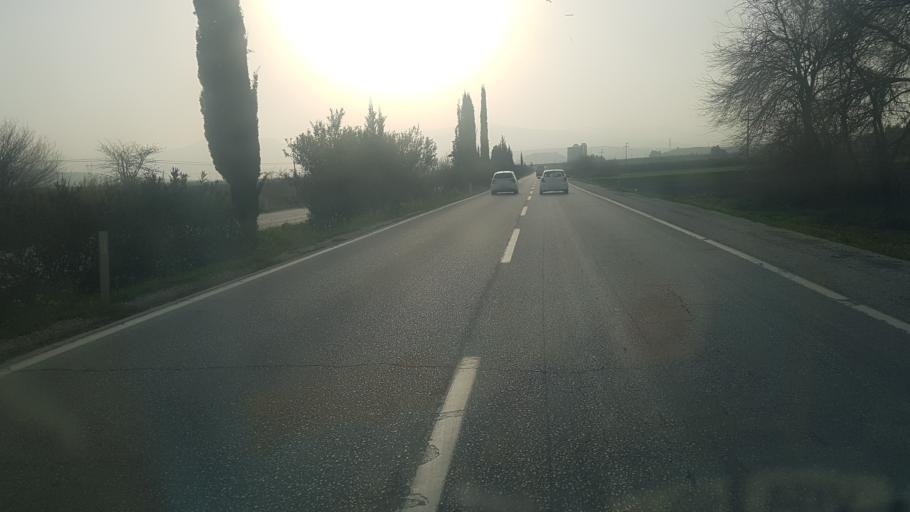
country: TR
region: Osmaniye
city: Toprakkale
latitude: 37.0674
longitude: 36.0991
